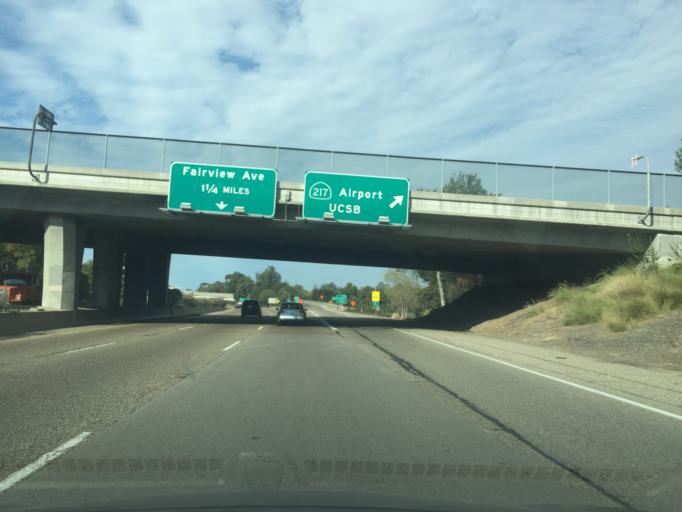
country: US
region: California
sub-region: Santa Barbara County
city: Goleta
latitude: 34.4420
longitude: -119.8077
